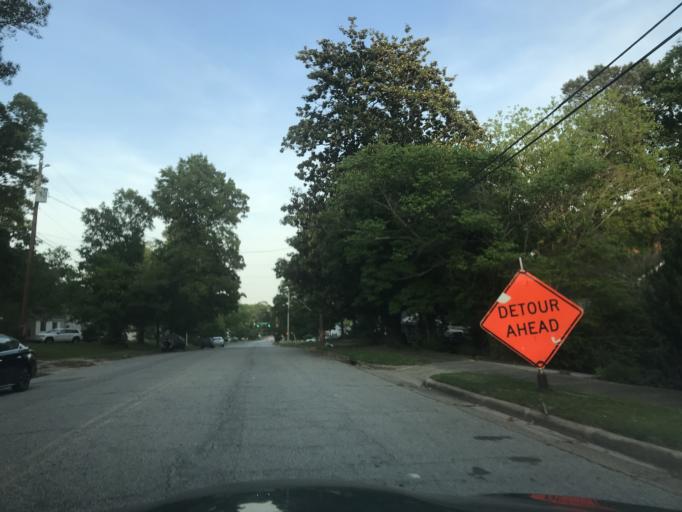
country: US
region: North Carolina
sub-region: Wake County
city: Raleigh
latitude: 35.7884
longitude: -78.6113
